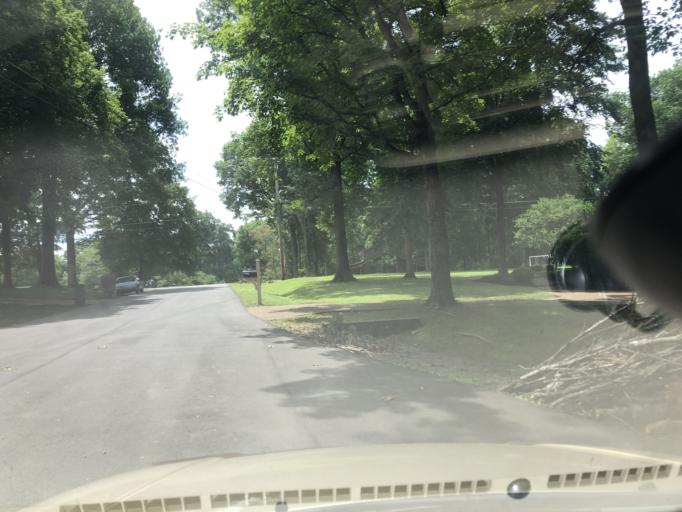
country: US
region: Tennessee
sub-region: Davidson County
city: Lakewood
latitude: 36.2577
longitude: -86.5877
